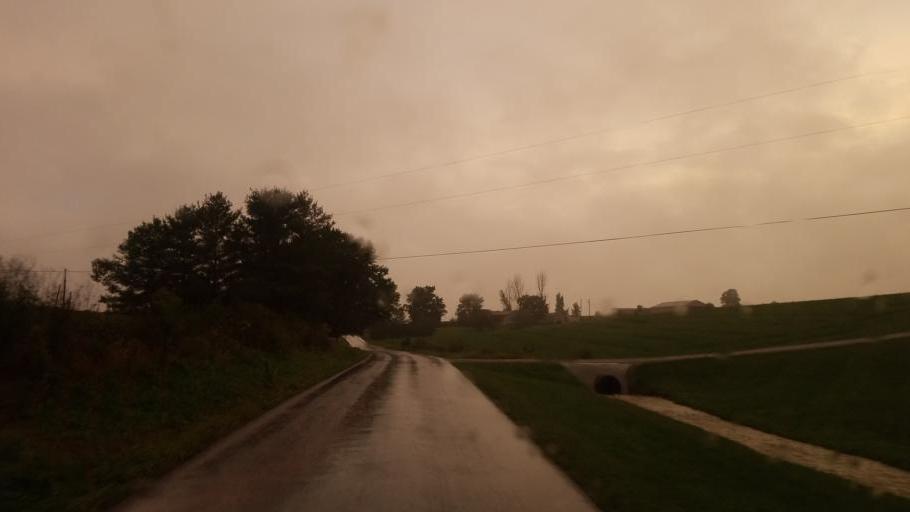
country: US
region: Kentucky
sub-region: Fleming County
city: Flemingsburg
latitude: 38.4617
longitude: -83.6422
